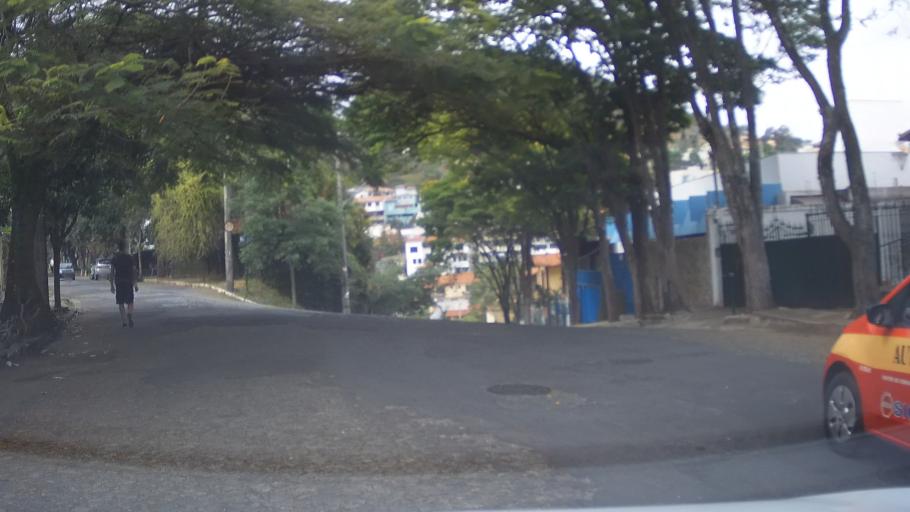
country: BR
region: Minas Gerais
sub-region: Belo Horizonte
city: Belo Horizonte
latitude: -19.9529
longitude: -43.9202
